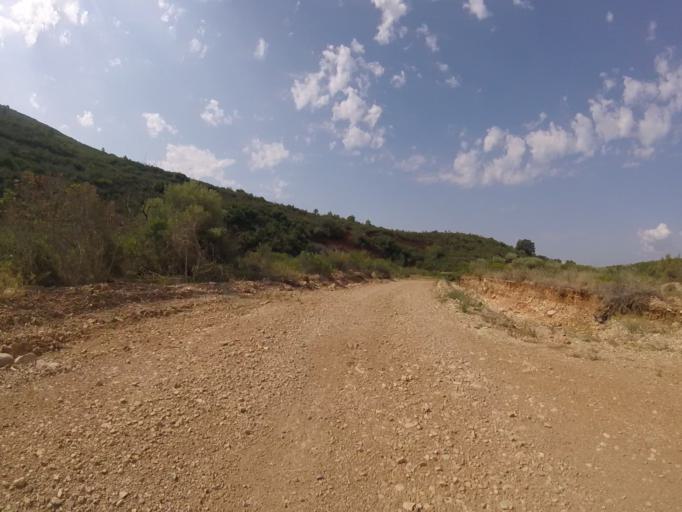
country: ES
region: Valencia
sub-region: Provincia de Castello
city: Alcala de Xivert
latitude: 40.3294
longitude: 0.1938
